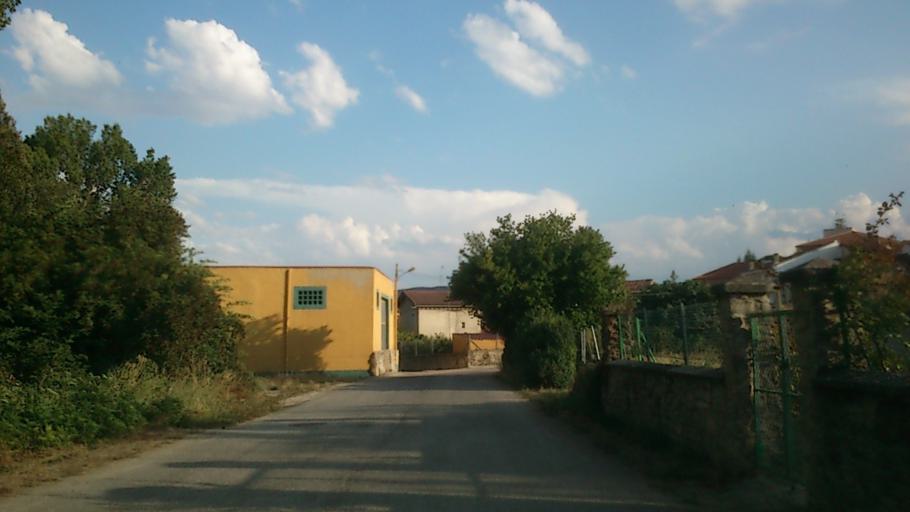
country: ES
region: Castille and Leon
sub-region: Provincia de Burgos
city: Frias
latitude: 42.7945
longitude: -3.2687
